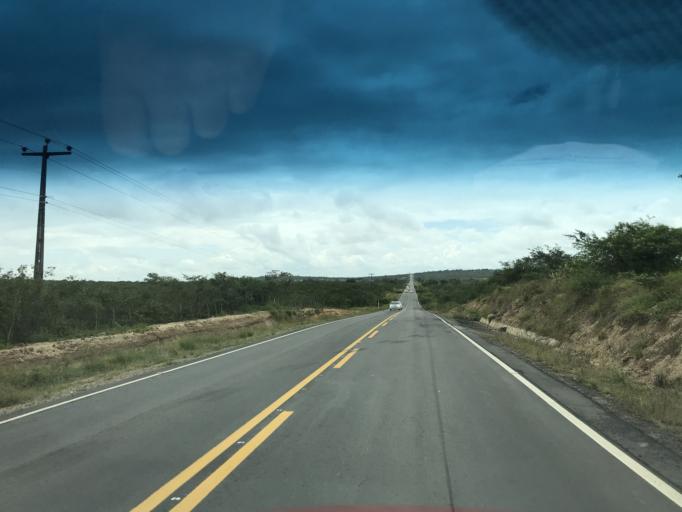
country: BR
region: Bahia
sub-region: Castro Alves
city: Castro Alves
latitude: -12.6798
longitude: -39.3022
